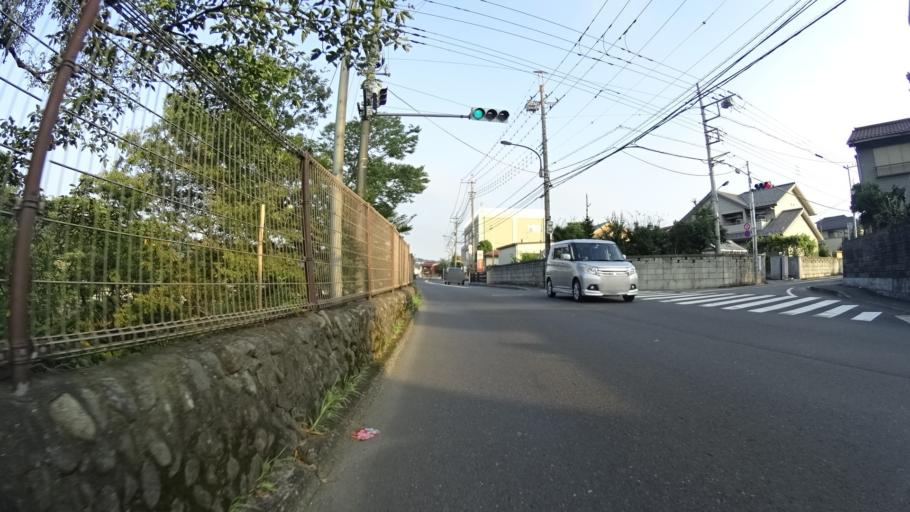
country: JP
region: Tokyo
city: Fussa
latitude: 35.7554
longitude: 139.3095
